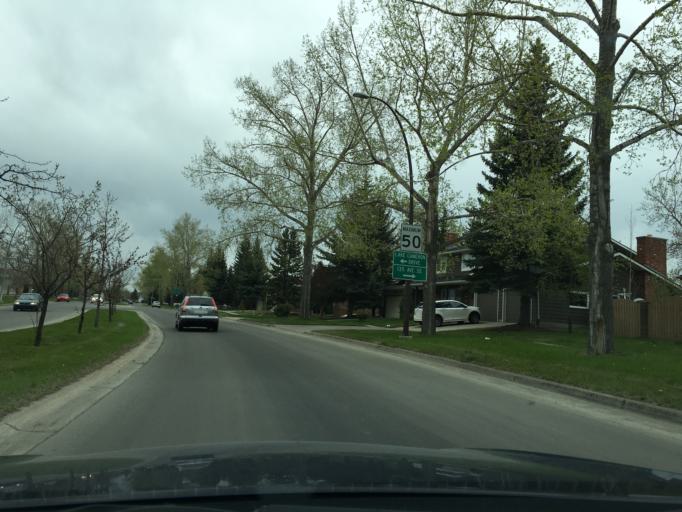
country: CA
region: Alberta
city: Calgary
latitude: 50.9311
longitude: -114.0627
